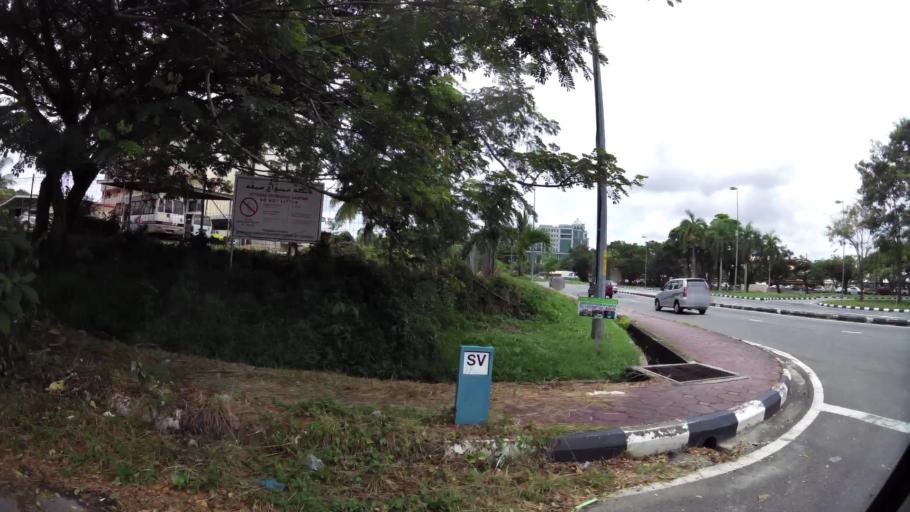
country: BN
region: Brunei and Muara
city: Bandar Seri Begawan
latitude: 4.9022
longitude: 114.9179
